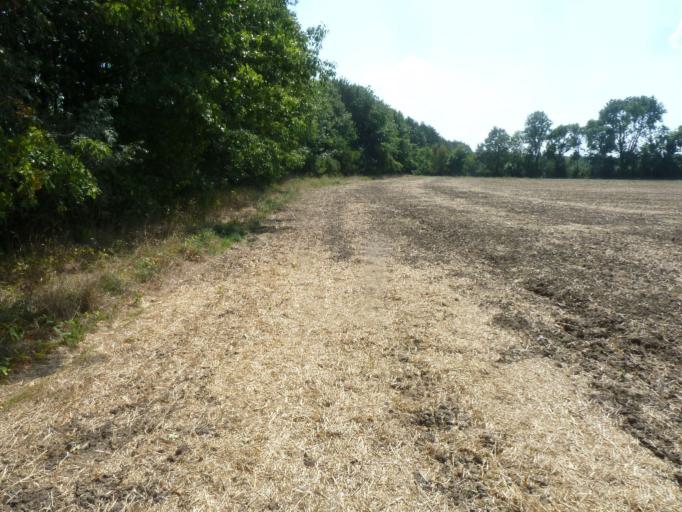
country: HU
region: Vas
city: Gencsapati
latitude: 47.2534
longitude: 16.5830
